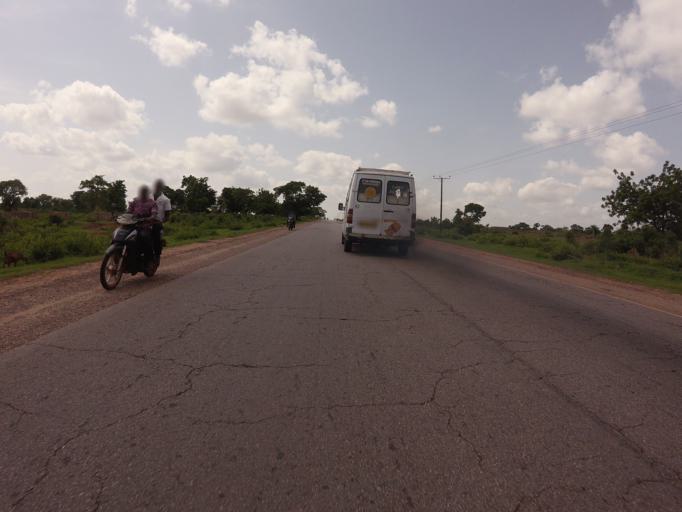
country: GH
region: Northern
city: Savelugu
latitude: 9.5807
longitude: -0.8337
